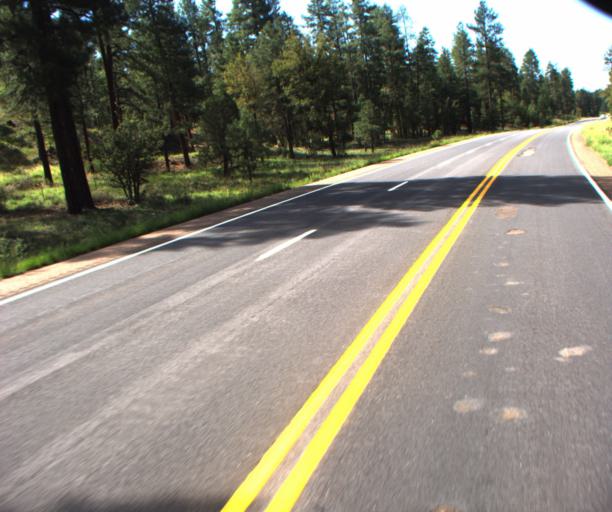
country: US
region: Arizona
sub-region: Navajo County
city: Show Low
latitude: 34.1851
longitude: -110.0925
